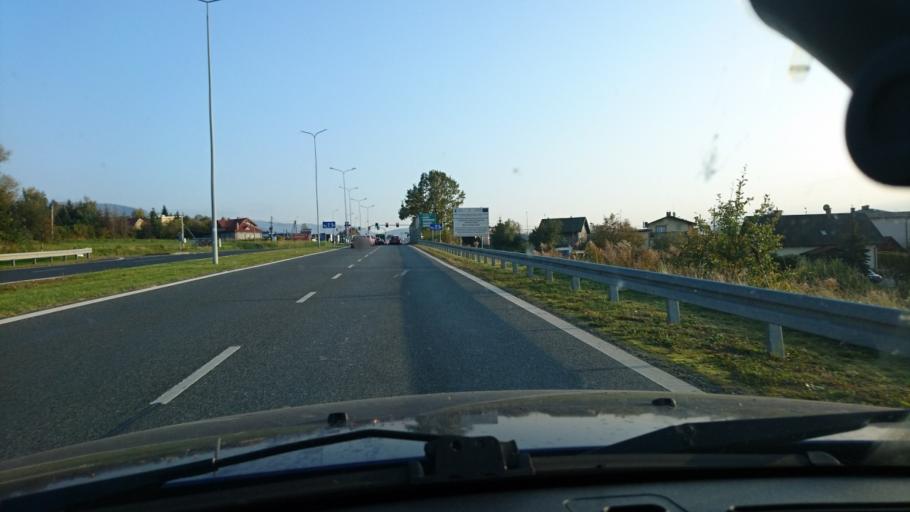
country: PL
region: Silesian Voivodeship
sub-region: Bielsko-Biala
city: Bielsko-Biala
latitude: 49.8407
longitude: 19.0699
